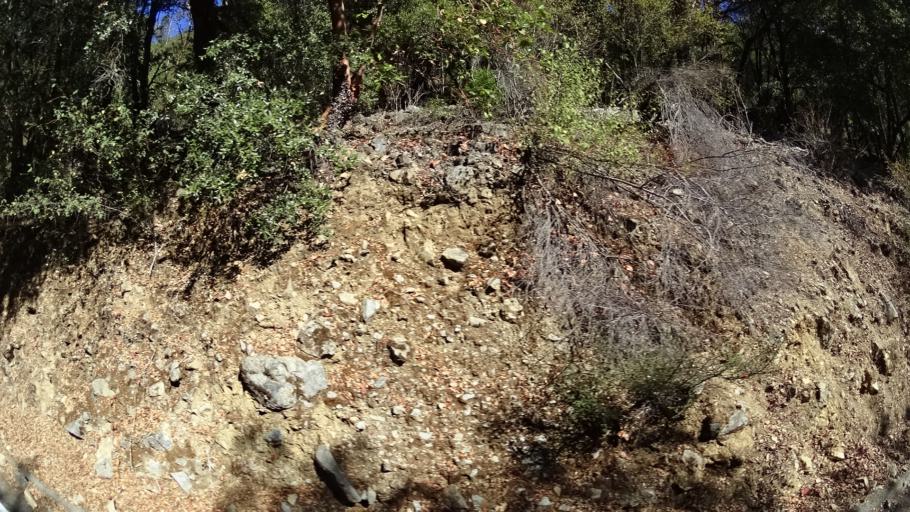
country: US
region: California
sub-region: Siskiyou County
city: Happy Camp
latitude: 41.3783
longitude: -123.4367
